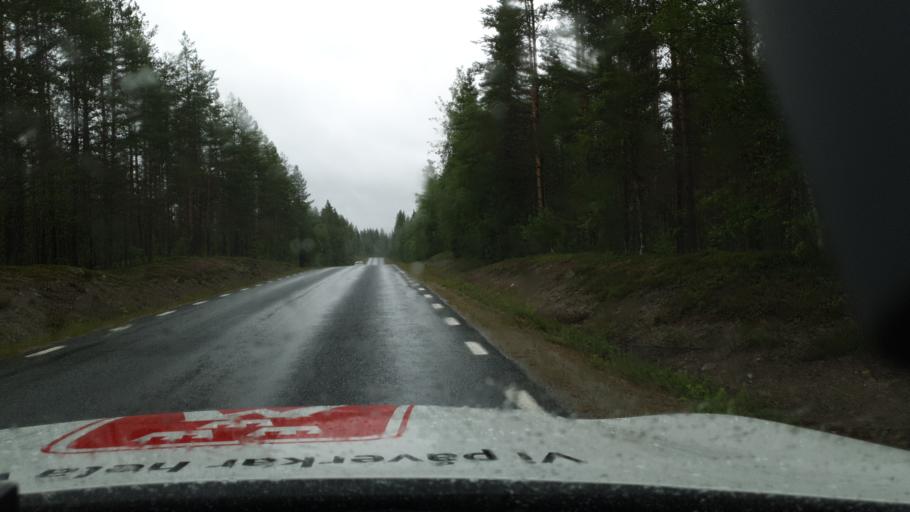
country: SE
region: Vaesterbotten
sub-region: Asele Kommun
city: Insjon
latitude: 64.2396
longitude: 17.5488
